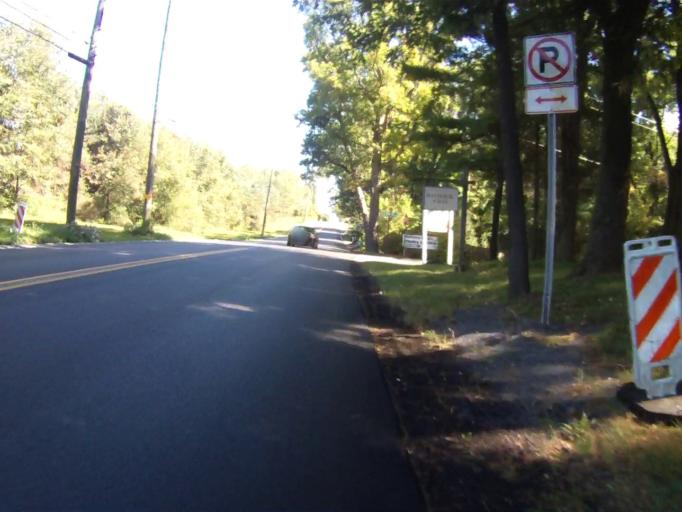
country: US
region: Pennsylvania
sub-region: Centre County
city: Park Forest Village
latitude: 40.8346
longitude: -77.8806
